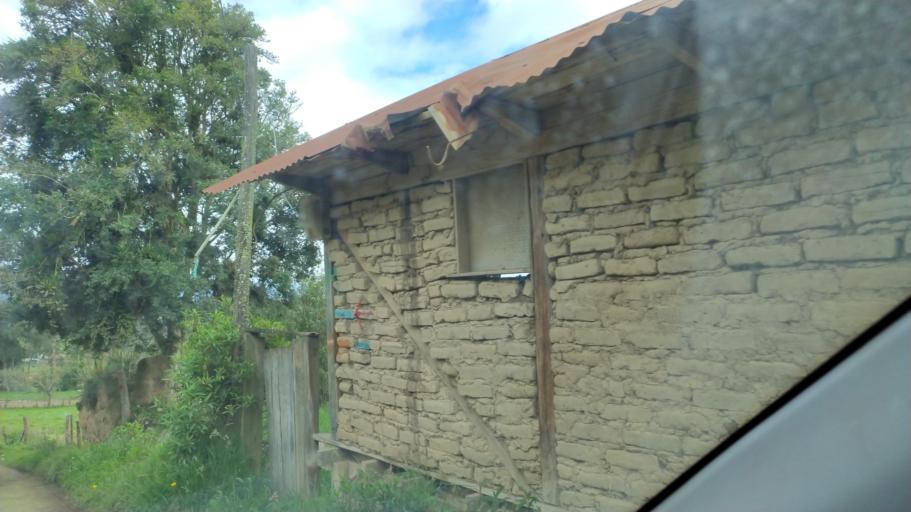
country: EC
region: Chimborazo
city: Riobamba
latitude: -1.6603
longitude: -78.5698
